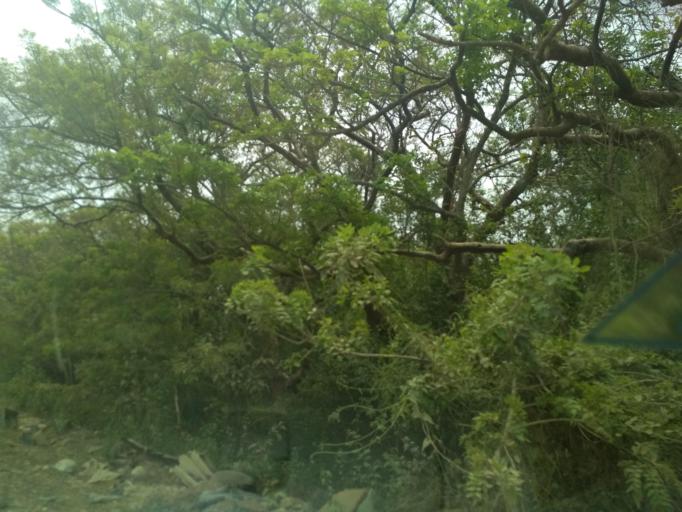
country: MX
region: Veracruz
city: Paso del Toro
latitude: 19.0406
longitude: -96.1506
